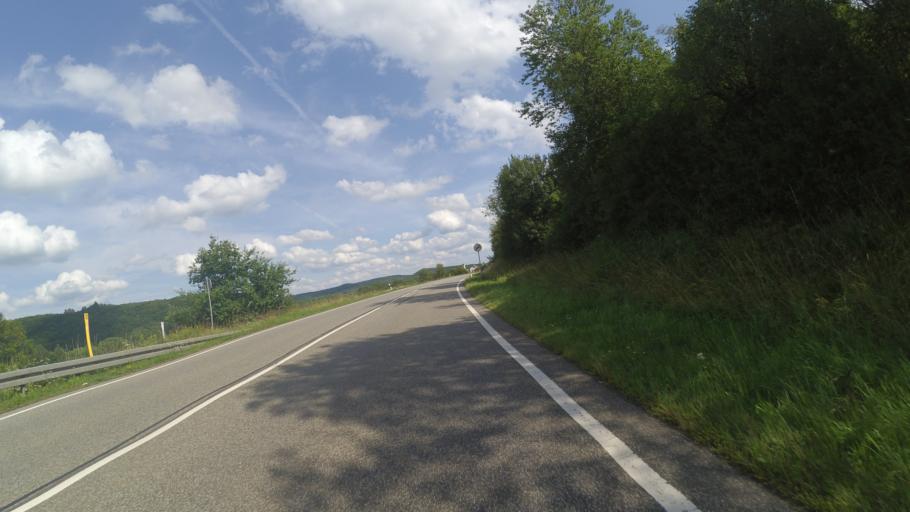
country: DE
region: Rheinland-Pfalz
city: Achtelsbach
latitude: 49.6027
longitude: 7.0502
